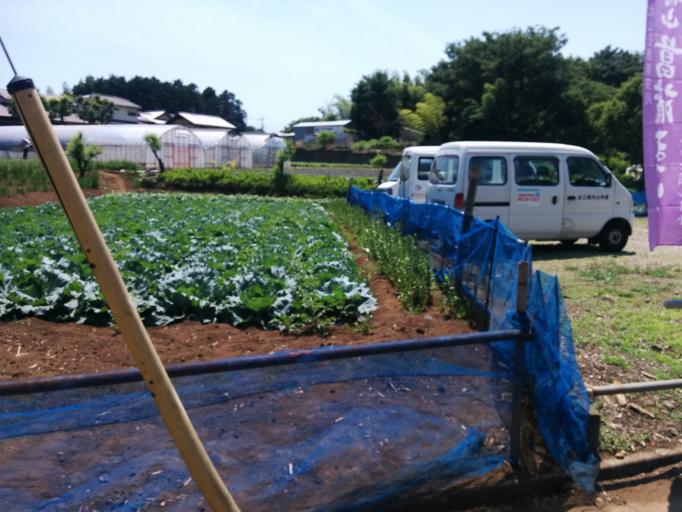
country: JP
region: Tokyo
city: Higashimurayama-shi
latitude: 35.7664
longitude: 139.4605
